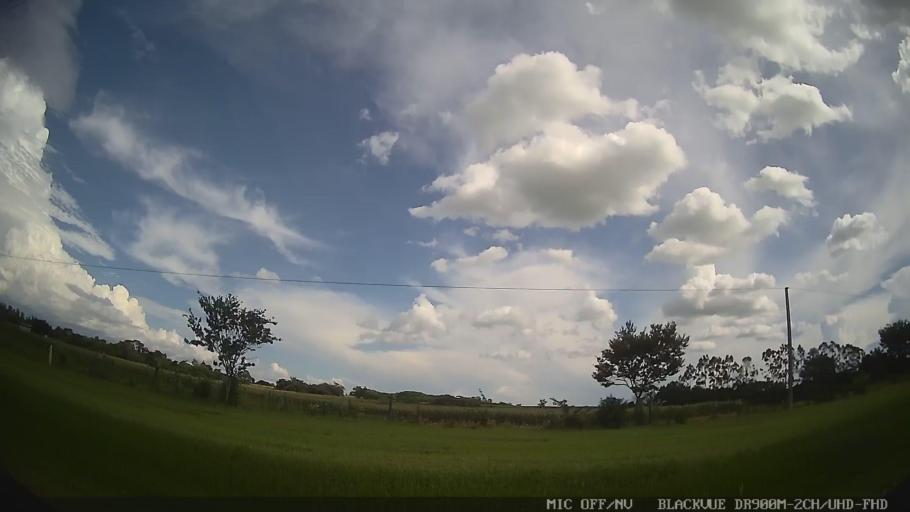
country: BR
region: Sao Paulo
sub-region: Laranjal Paulista
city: Laranjal Paulista
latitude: -23.0462
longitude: -47.9194
